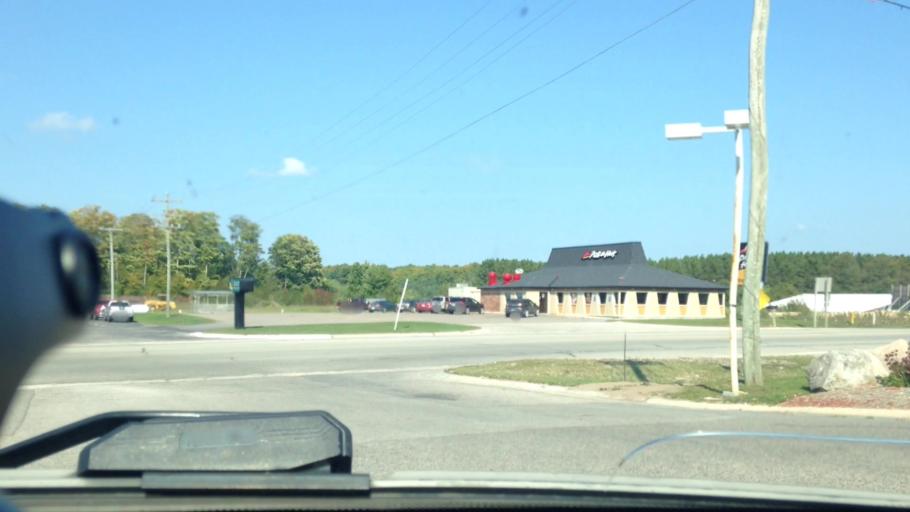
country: US
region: Michigan
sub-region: Luce County
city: Newberry
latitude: 46.3030
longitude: -85.5084
